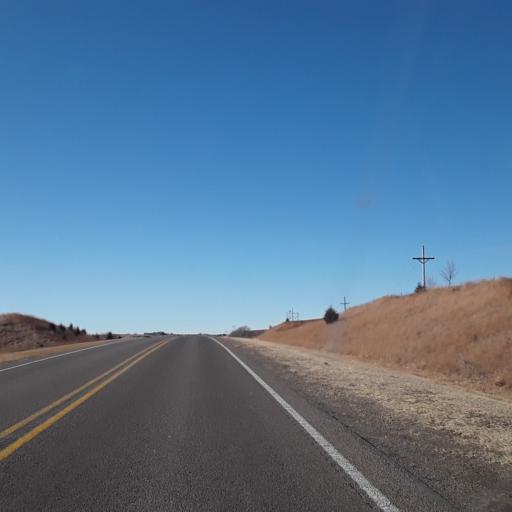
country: US
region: Nebraska
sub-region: Frontier County
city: Stockville
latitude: 40.6288
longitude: -100.5424
